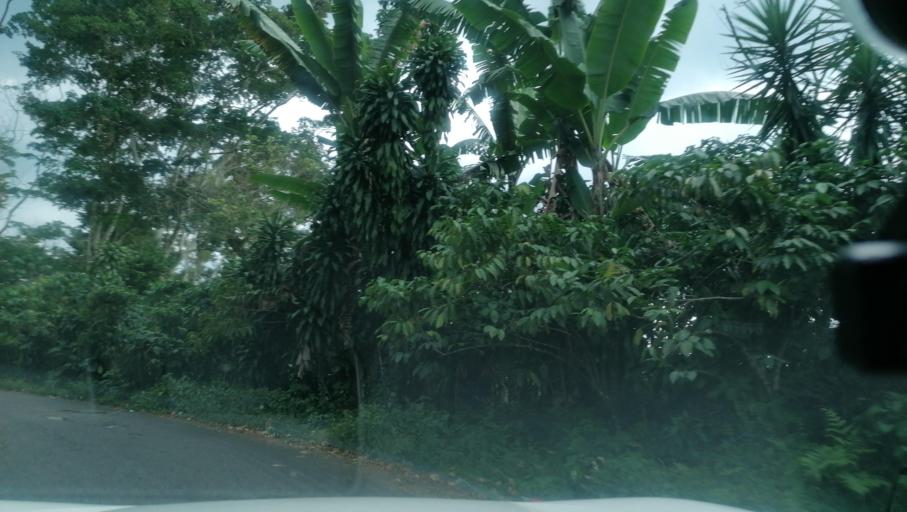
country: MX
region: Chiapas
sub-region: Cacahoatan
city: Benito Juarez
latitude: 15.0715
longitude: -92.1914
